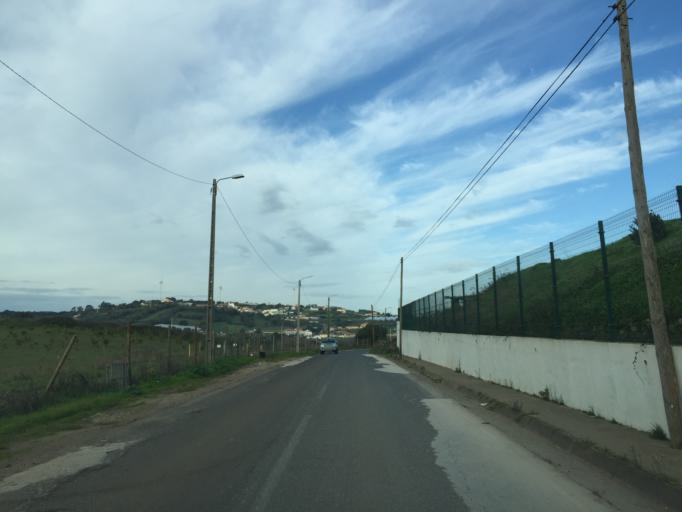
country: PT
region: Lisbon
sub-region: Odivelas
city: Canecas
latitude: 38.8289
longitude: -9.2484
